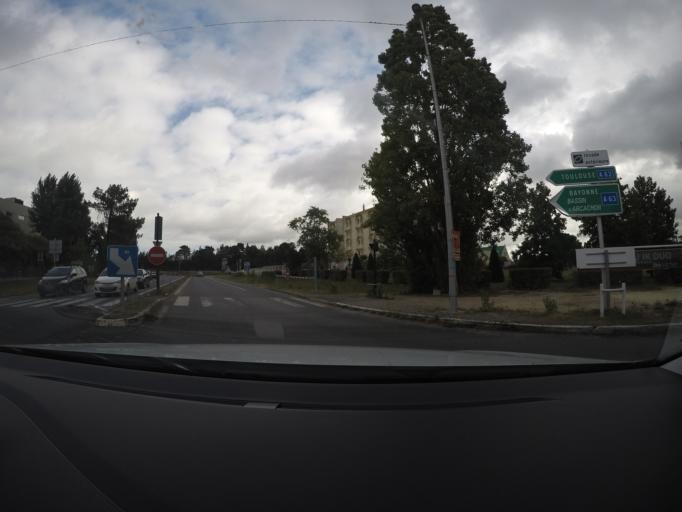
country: FR
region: Aquitaine
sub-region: Departement de la Gironde
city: Pessac
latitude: 44.7882
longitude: -0.6464
